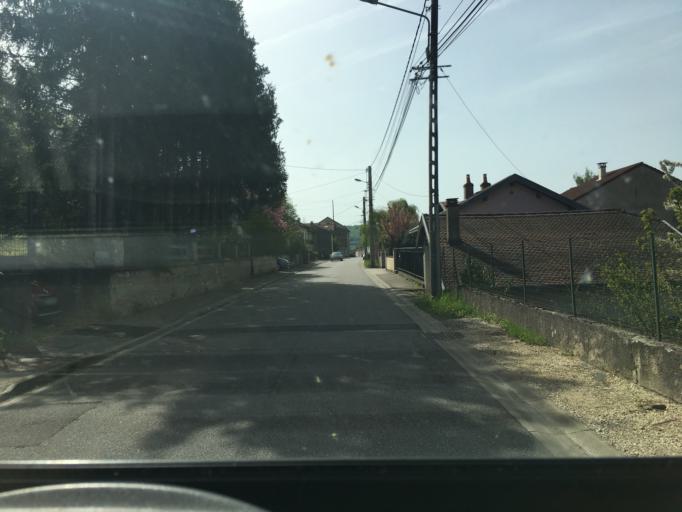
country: FR
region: Lorraine
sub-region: Departement de Meurthe-et-Moselle
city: Chaligny
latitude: 48.6383
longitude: 6.0448
